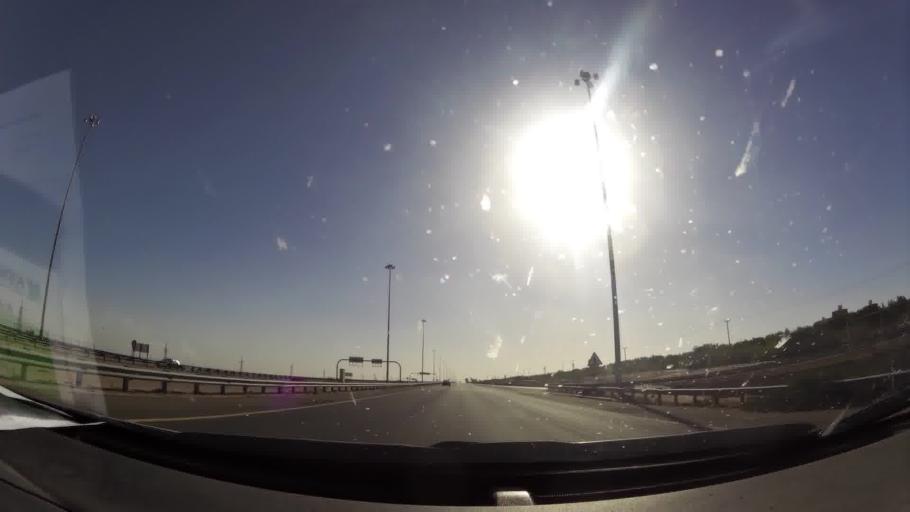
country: KW
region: Muhafazat al Jahra'
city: Al Jahra'
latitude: 29.4726
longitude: 47.7672
